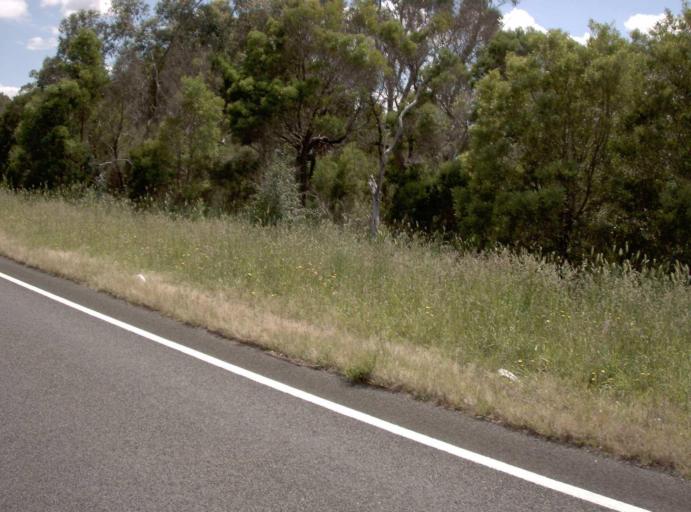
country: AU
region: Victoria
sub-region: Cardinia
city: Koo-Wee-Rup
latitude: -38.3674
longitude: 145.5633
